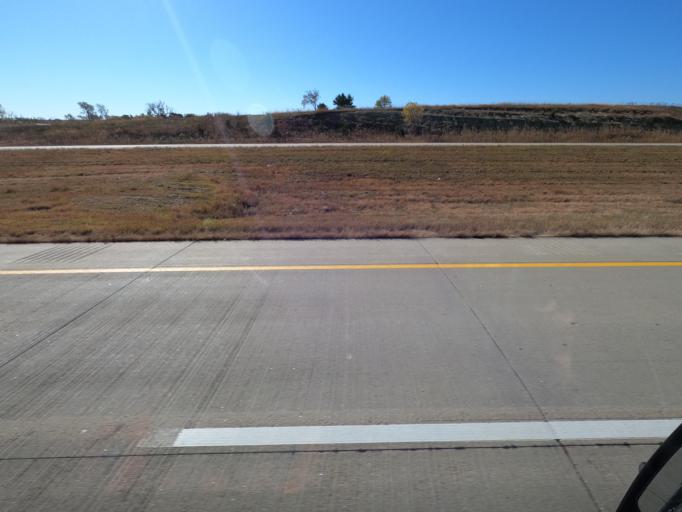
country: US
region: Kansas
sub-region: Wabaunsee County
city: Alma
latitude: 39.0664
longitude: -96.3044
